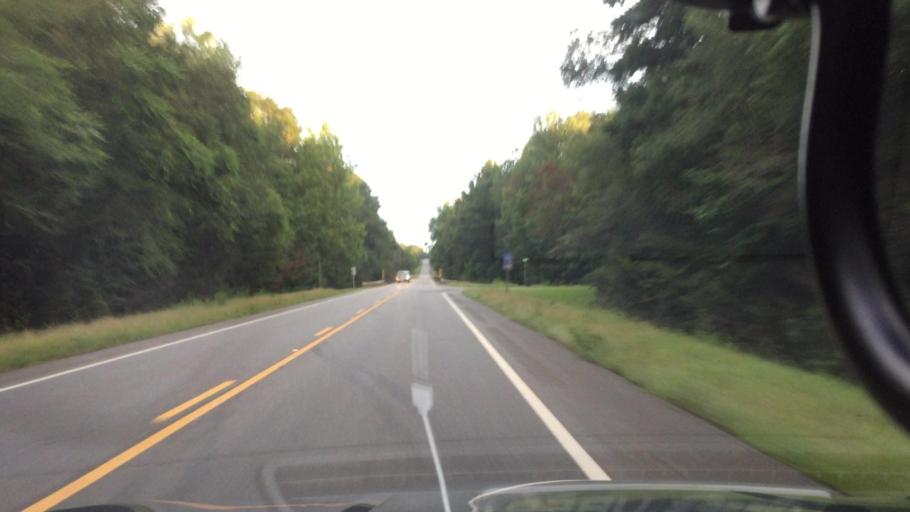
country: US
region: Alabama
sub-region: Pike County
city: Brundidge
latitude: 31.5900
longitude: -85.9416
